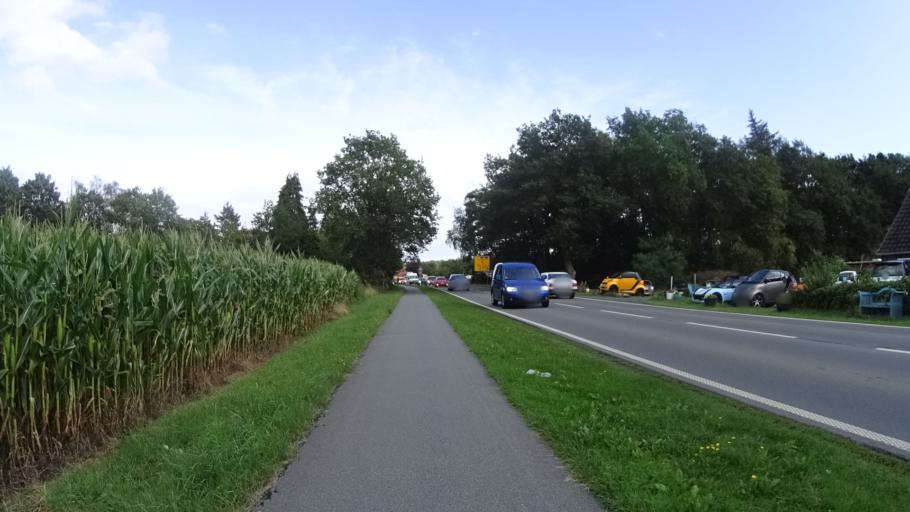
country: DE
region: Lower Saxony
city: Bockhorn
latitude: 53.3855
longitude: 8.0530
